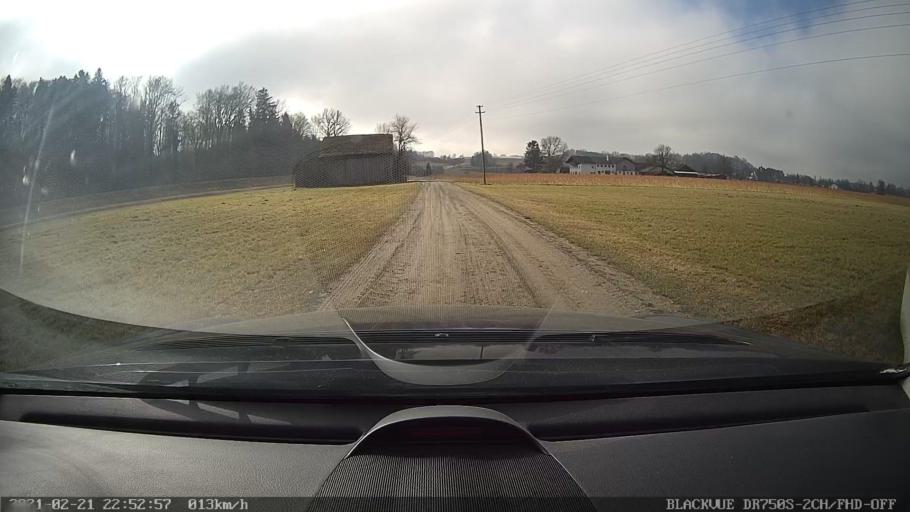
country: DE
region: Bavaria
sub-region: Upper Bavaria
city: Griesstatt
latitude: 48.0131
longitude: 12.1879
